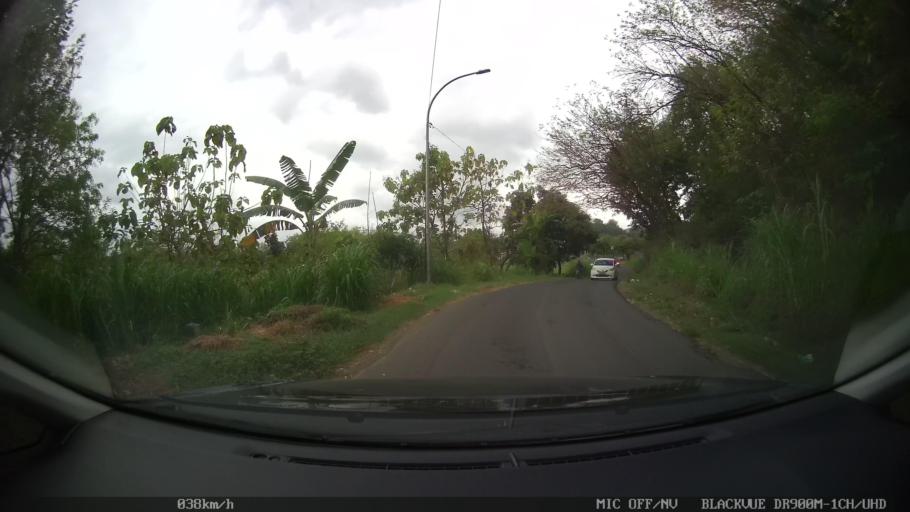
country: ID
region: Daerah Istimewa Yogyakarta
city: Sewon
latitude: -7.8615
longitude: 110.4218
